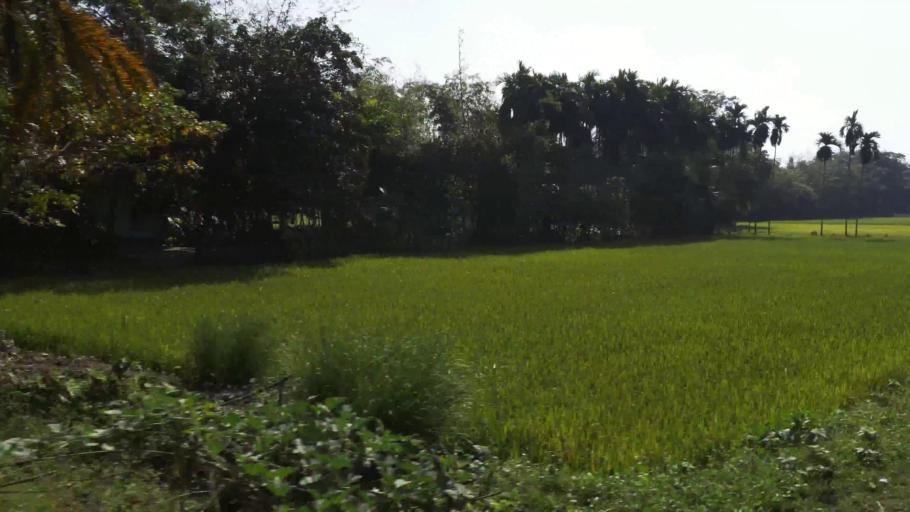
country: BD
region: Dhaka
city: Gafargaon
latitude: 24.5016
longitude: 90.5199
